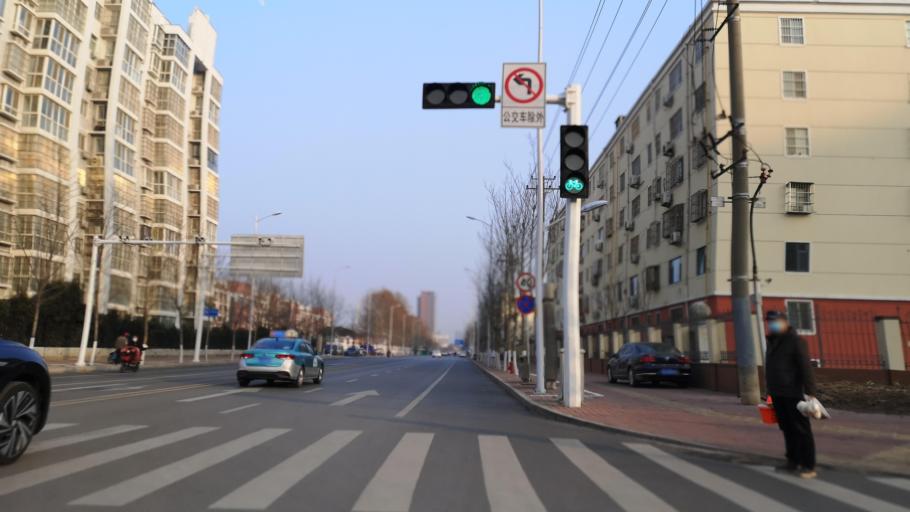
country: CN
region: Henan Sheng
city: Zhongyuanlu
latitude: 35.7640
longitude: 115.0572
